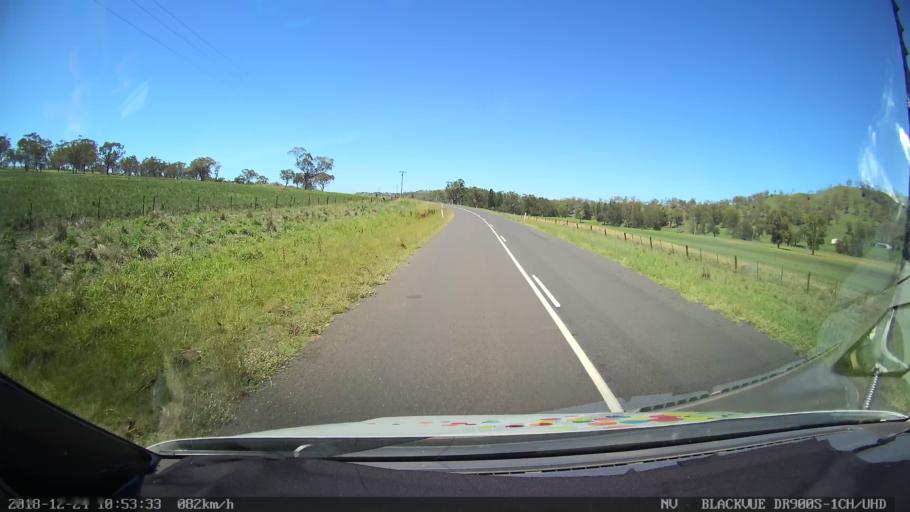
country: AU
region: New South Wales
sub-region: Upper Hunter Shire
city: Merriwa
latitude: -31.9928
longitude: 150.4203
